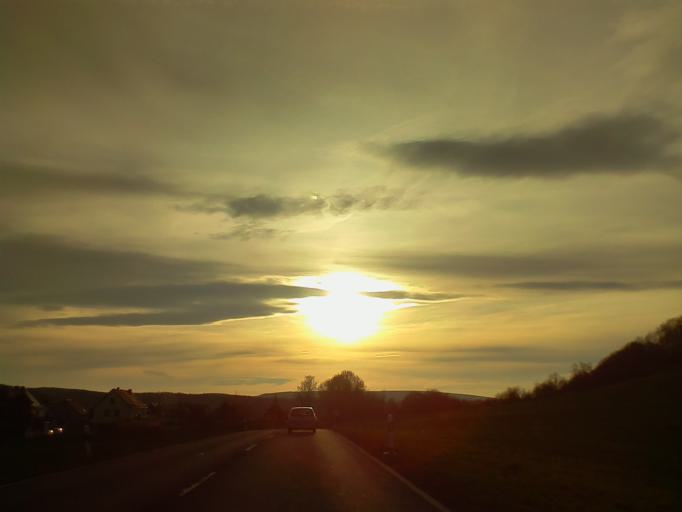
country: DE
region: Thuringia
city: Freienorla
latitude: 50.7796
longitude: 11.5501
